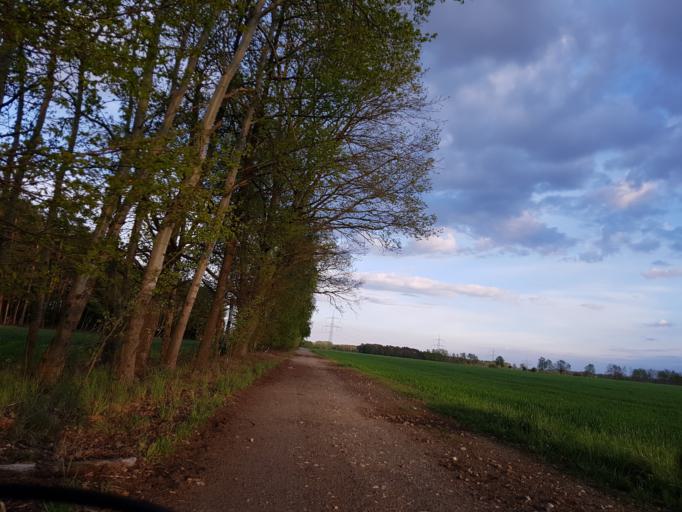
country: DE
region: Brandenburg
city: Schilda
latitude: 51.5696
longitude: 13.3828
